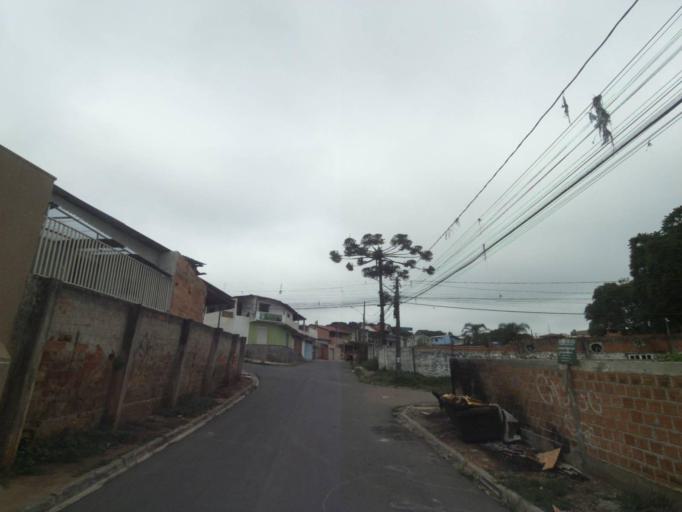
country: BR
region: Parana
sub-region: Curitiba
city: Curitiba
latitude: -25.4996
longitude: -49.3505
